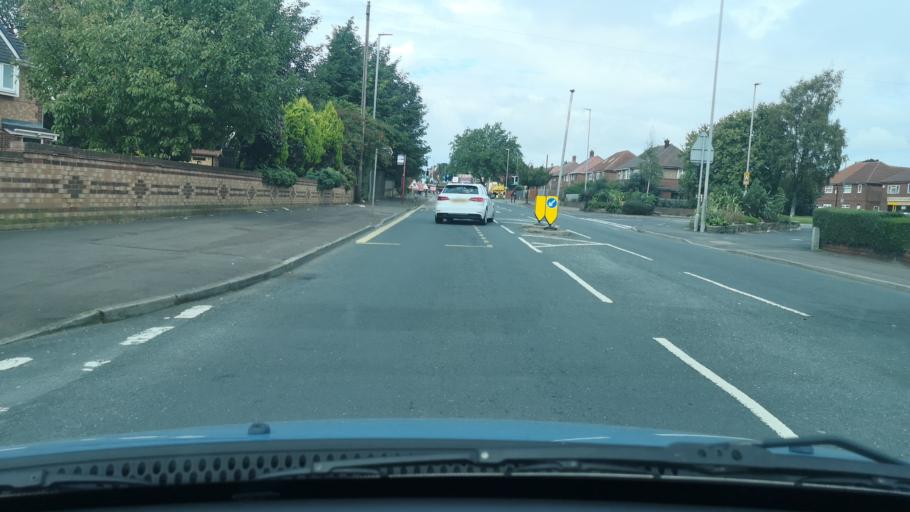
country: GB
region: England
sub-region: Kirklees
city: Batley
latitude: 53.7037
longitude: -1.6469
